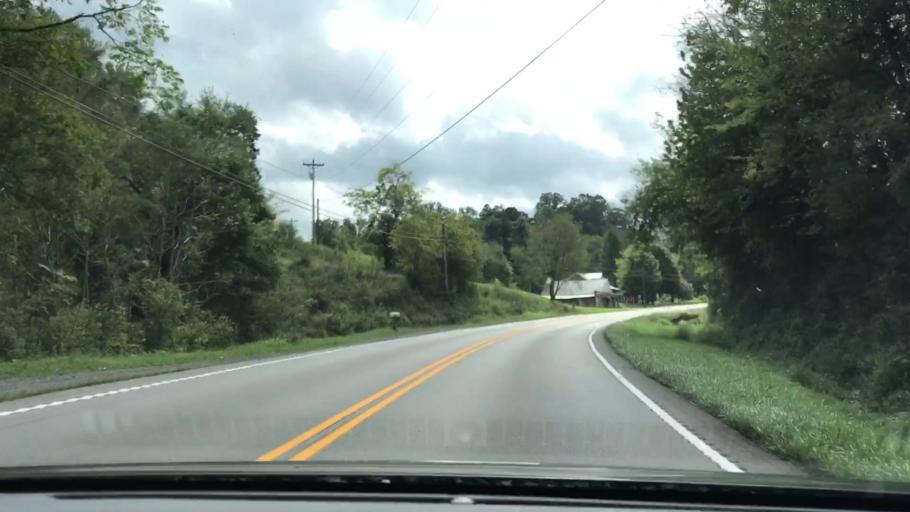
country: US
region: Kentucky
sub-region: Cumberland County
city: Burkesville
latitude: 36.8061
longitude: -85.4267
